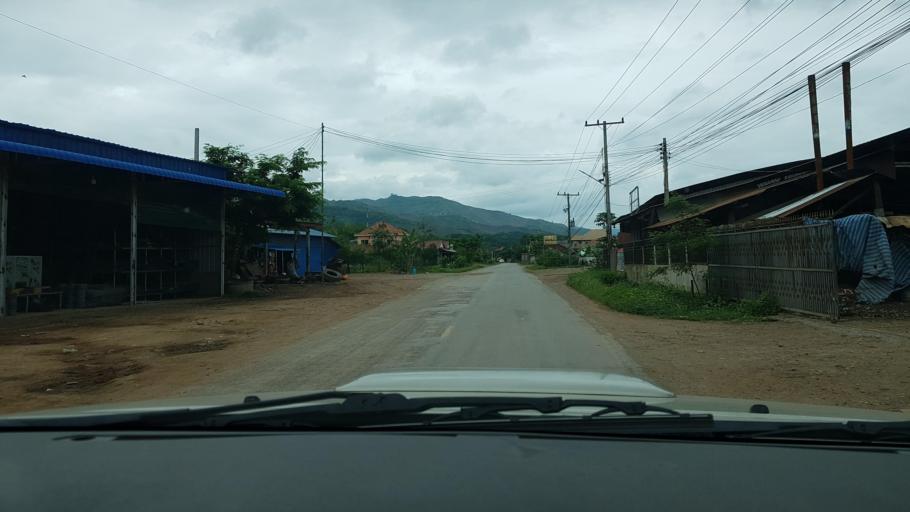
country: LA
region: Loungnamtha
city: Muang Nale
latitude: 20.2966
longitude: 101.6358
